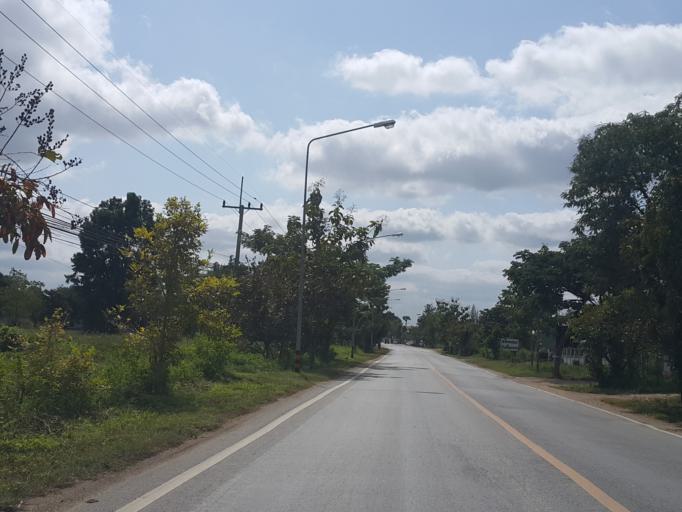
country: TH
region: Lamphun
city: Ban Thi
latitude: 18.5984
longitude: 99.0839
